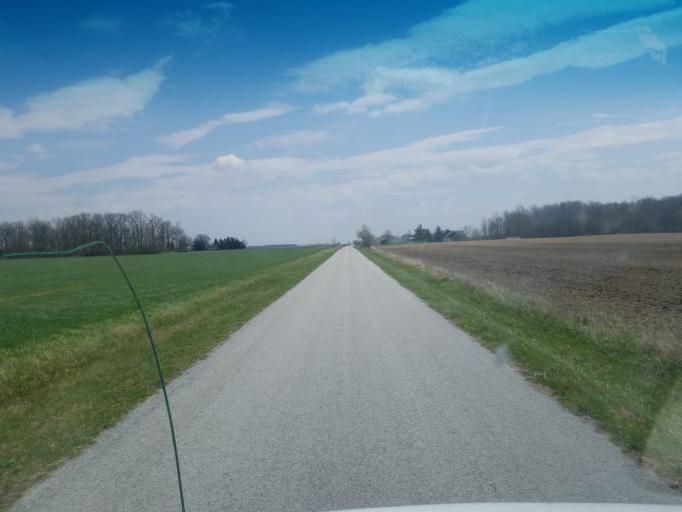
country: US
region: Ohio
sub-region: Hardin County
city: Forest
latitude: 40.7743
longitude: -83.4713
